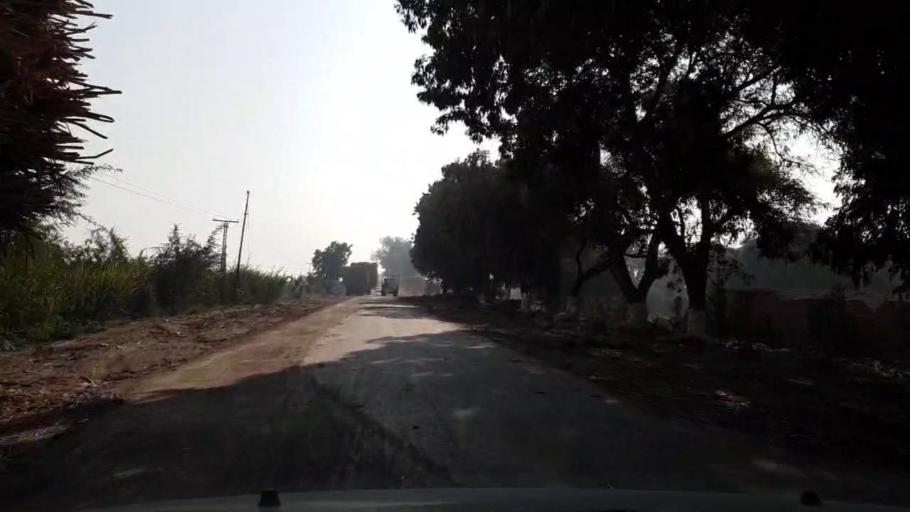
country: PK
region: Sindh
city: Matiari
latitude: 25.5778
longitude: 68.5017
